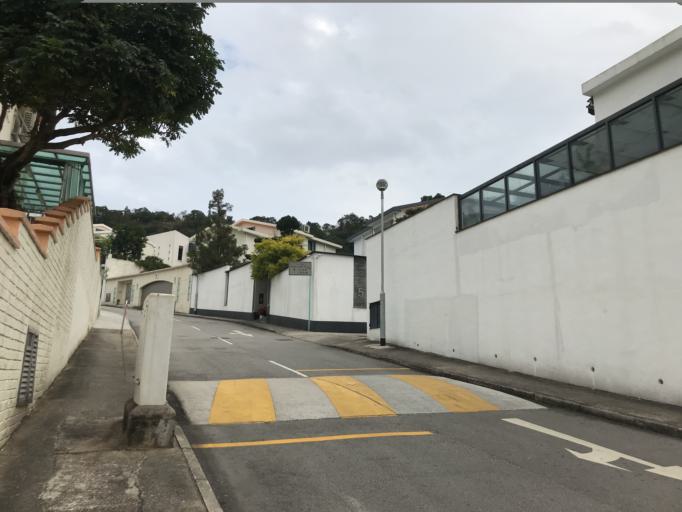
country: HK
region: Tai Po
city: Tai Po
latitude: 22.4631
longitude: 114.1603
